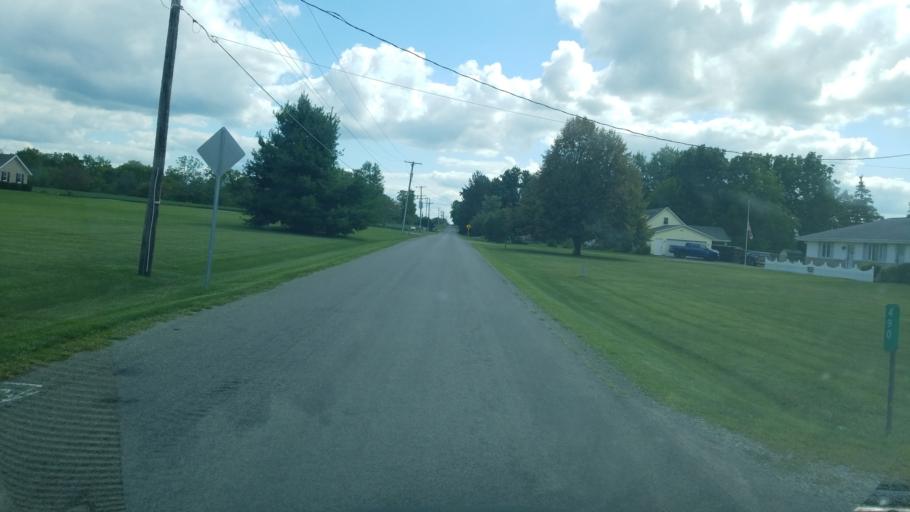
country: US
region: Ohio
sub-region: Allen County
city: Lima
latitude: 40.7347
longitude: -83.9942
